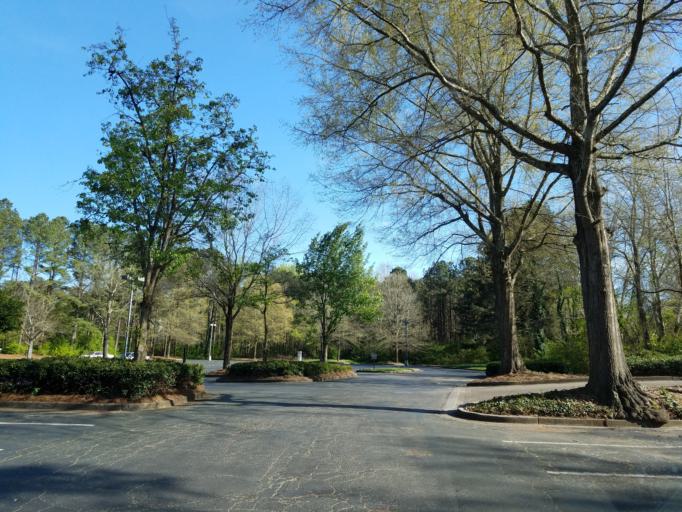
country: US
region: Georgia
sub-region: Cobb County
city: Smyrna
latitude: 33.9283
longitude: -84.4796
